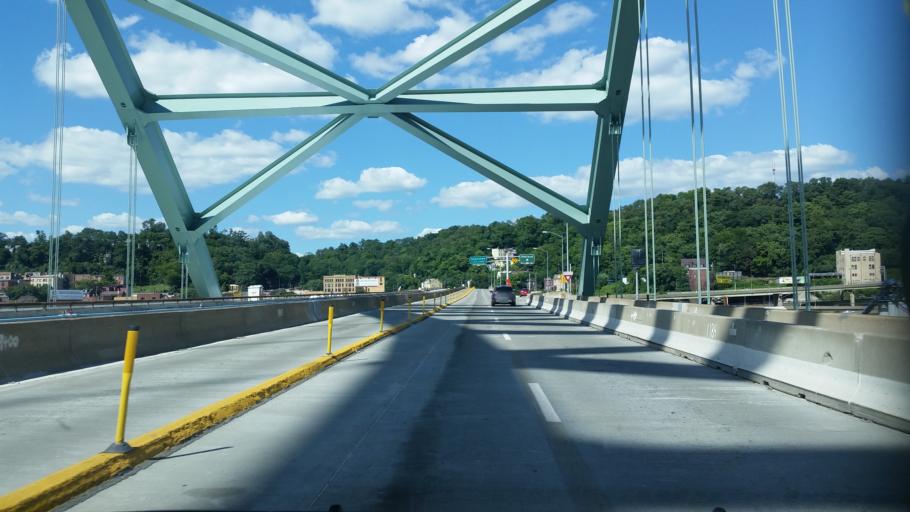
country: US
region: Pennsylvania
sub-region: Allegheny County
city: Pittsburgh
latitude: 40.4334
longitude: -79.9734
